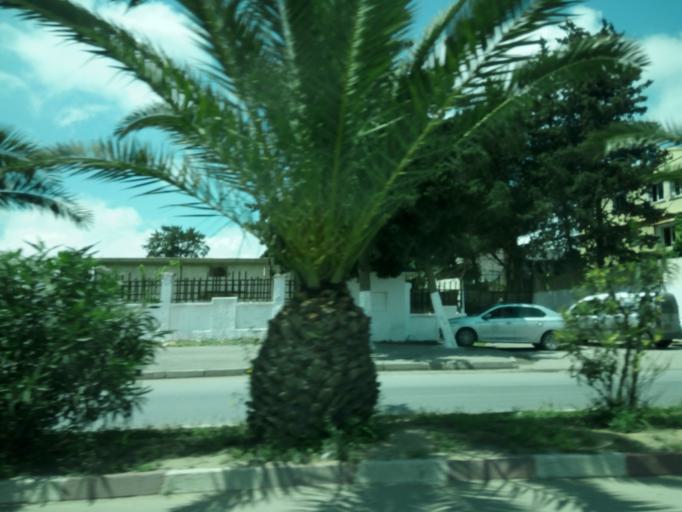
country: DZ
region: Tipaza
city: Saoula
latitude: 36.7296
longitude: 2.9920
